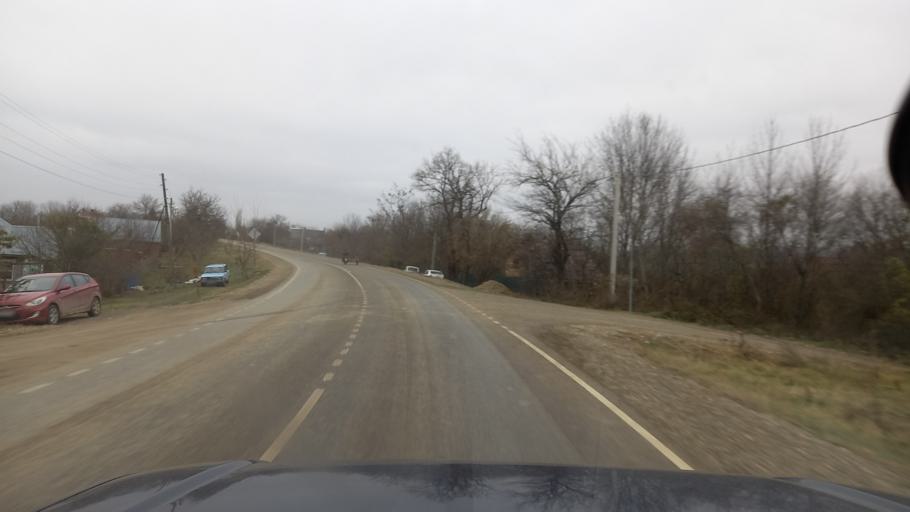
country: RU
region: Krasnodarskiy
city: Goryachiy Klyuch
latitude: 44.5268
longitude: 39.2919
